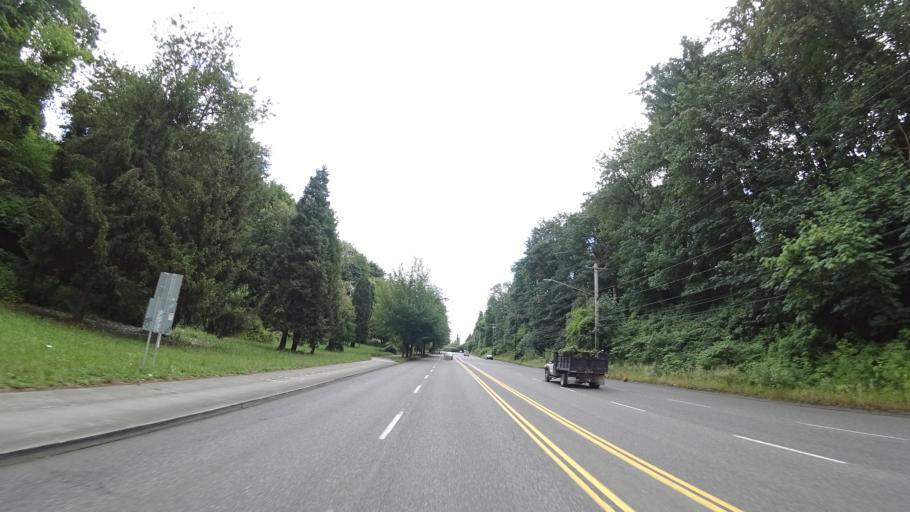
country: US
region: Oregon
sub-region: Multnomah County
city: Portland
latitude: 45.5560
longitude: -122.6896
